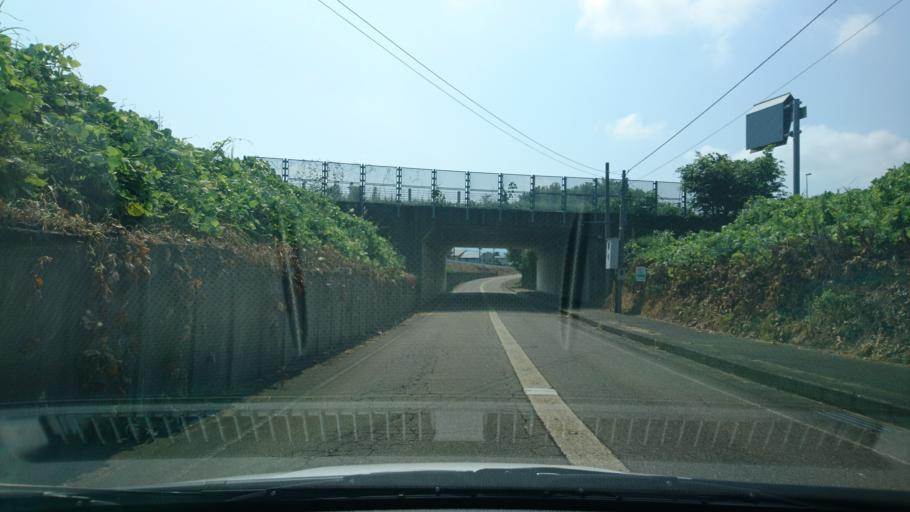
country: JP
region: Niigata
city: Arai
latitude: 37.0565
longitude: 138.2542
